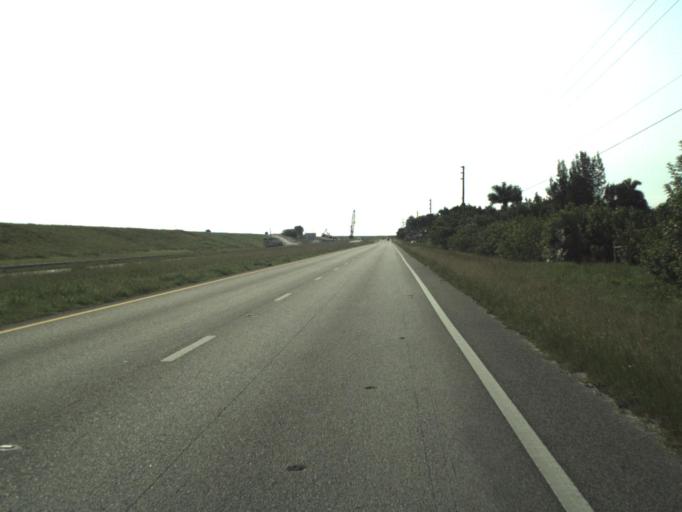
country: US
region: Florida
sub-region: Hendry County
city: Clewiston
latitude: 26.7309
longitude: -80.8599
